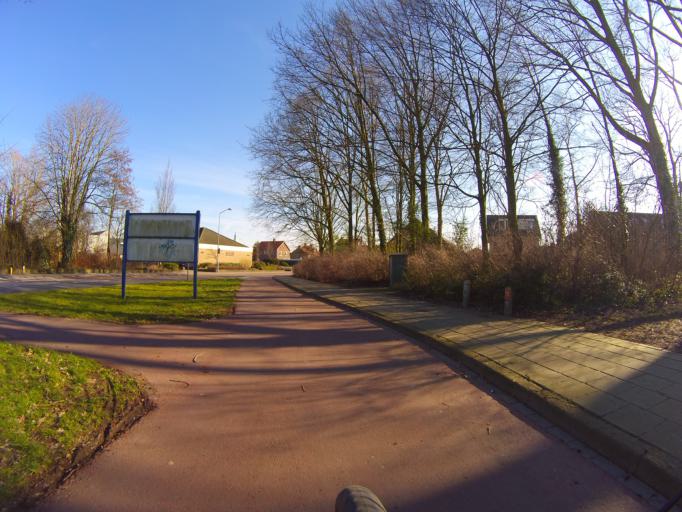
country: NL
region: Gelderland
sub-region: Gemeente Nijkerk
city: Nijkerk
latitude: 52.2263
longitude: 5.4770
